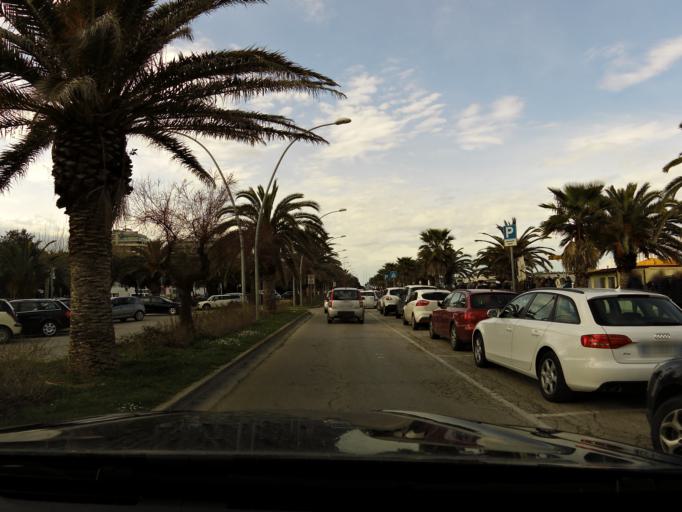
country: IT
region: The Marches
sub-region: Provincia di Macerata
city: Portocivitanova
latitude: 43.3070
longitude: 13.7342
